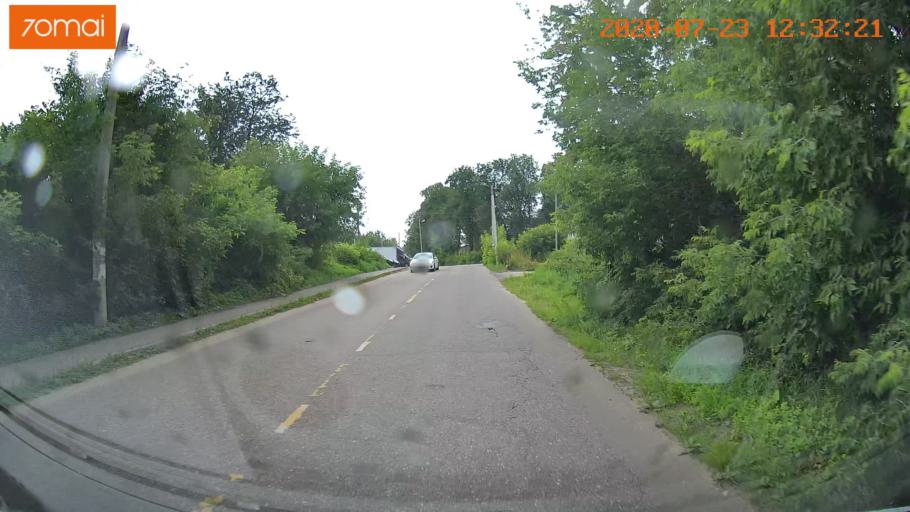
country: RU
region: Ivanovo
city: Bogorodskoye
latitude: 57.0460
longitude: 41.0076
